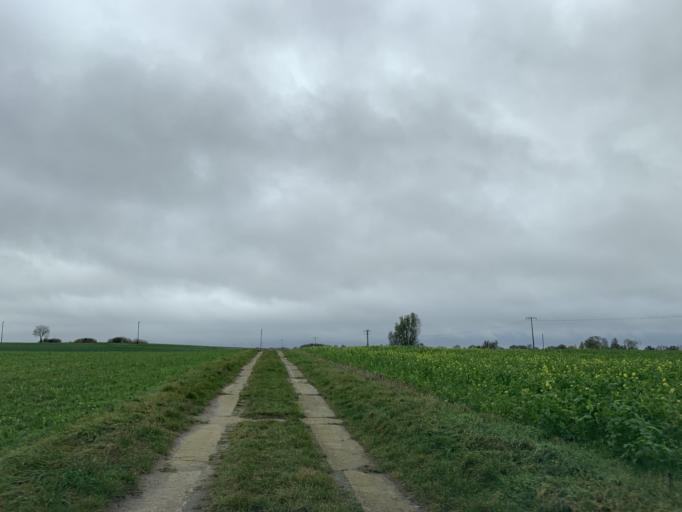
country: DE
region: Mecklenburg-Vorpommern
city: Blankensee
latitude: 53.3819
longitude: 13.2766
